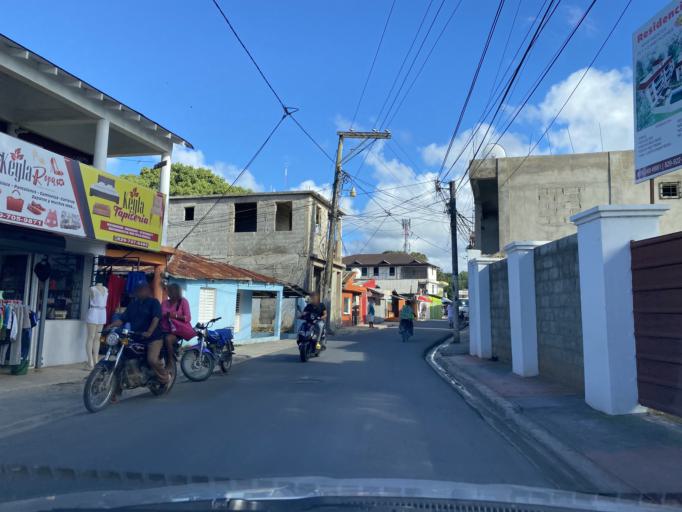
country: DO
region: Samana
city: Las Terrenas
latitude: 19.3138
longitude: -69.5432
